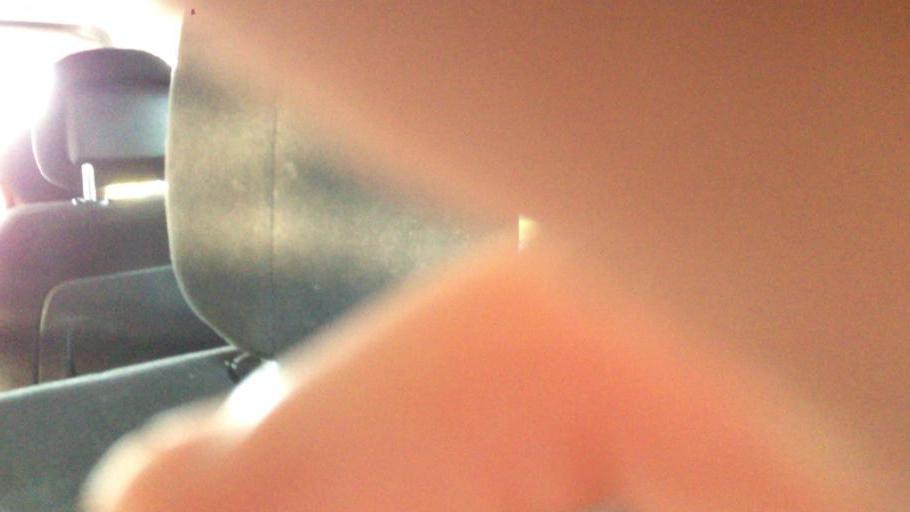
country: US
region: New York
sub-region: Dutchess County
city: Rhinebeck
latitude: 41.9388
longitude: -73.9082
